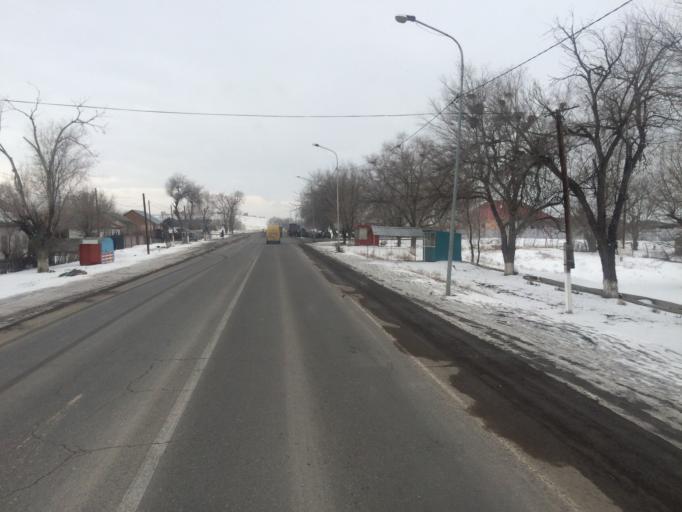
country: KG
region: Chuy
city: Bystrovka
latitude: 43.3308
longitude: 75.8360
